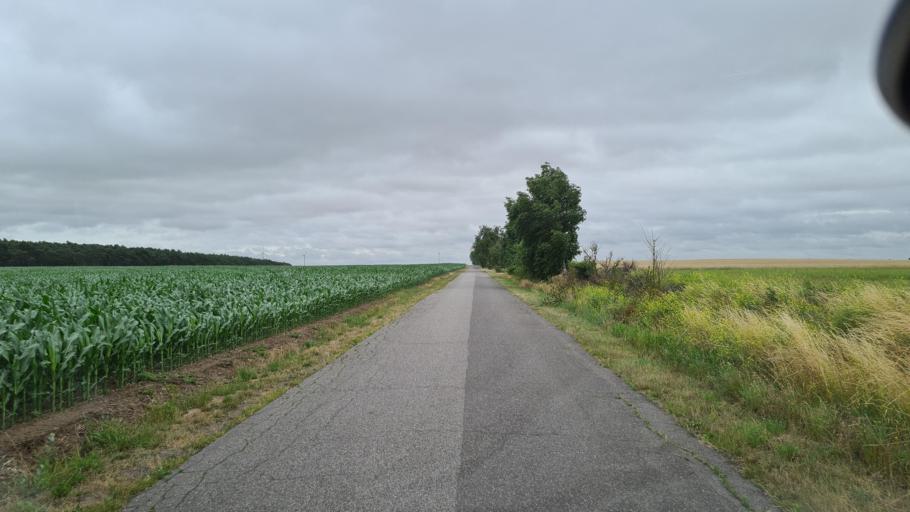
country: DE
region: Brandenburg
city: Juterbog
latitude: 51.9480
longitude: 13.1859
